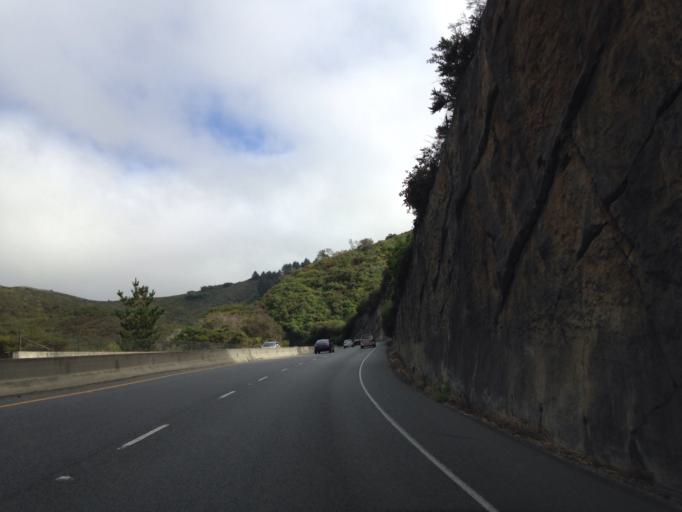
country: US
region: California
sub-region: San Mateo County
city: Highlands-Baywood Park
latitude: 37.4877
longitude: -122.3731
